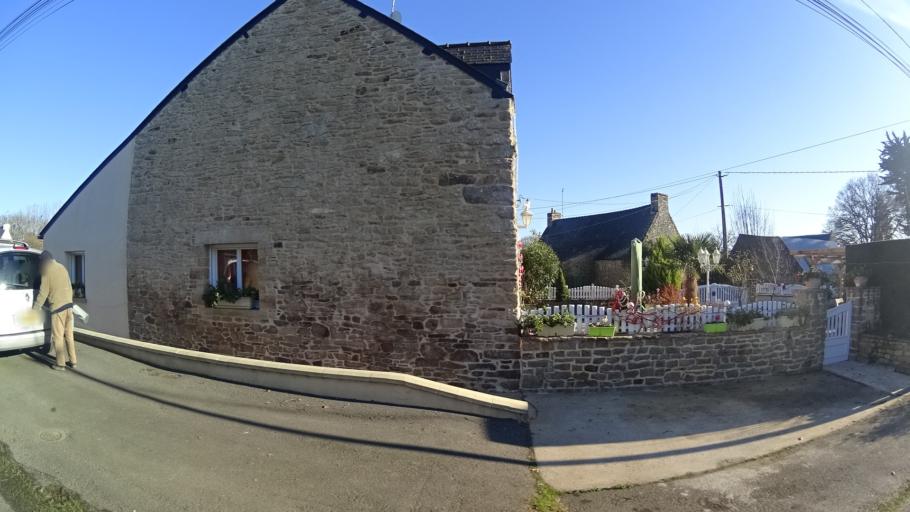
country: FR
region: Brittany
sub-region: Departement du Morbihan
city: Allaire
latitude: 47.6431
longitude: -2.1727
